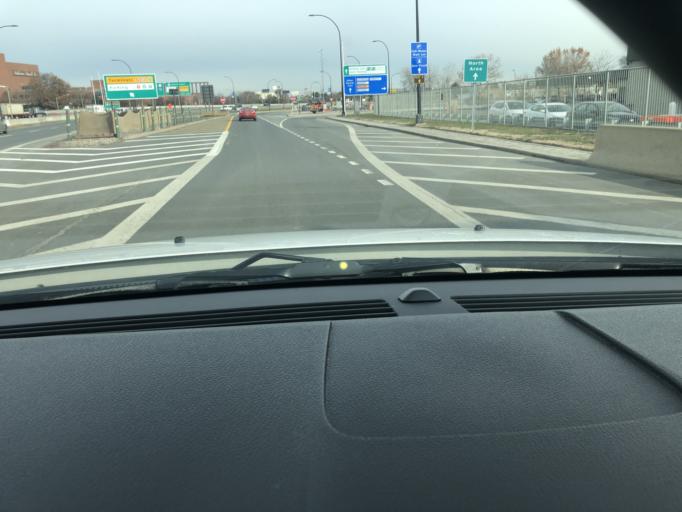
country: US
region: New Jersey
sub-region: Union County
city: Elizabeth
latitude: 40.6890
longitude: -74.1910
